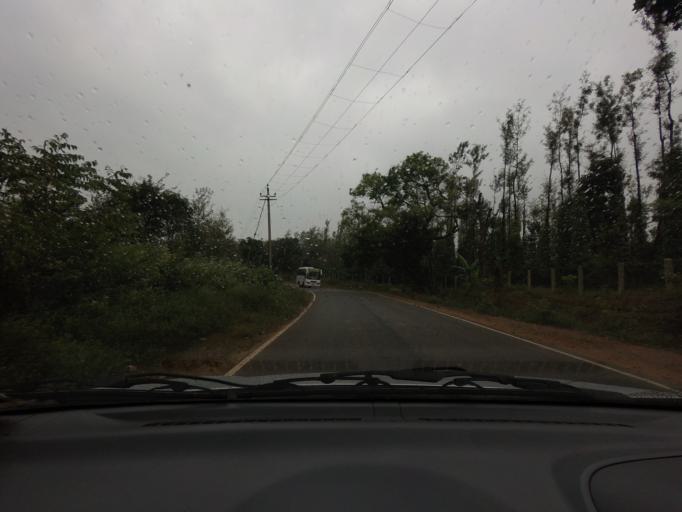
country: IN
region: Karnataka
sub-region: Hassan
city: Sakleshpur
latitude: 12.9892
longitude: 75.7130
